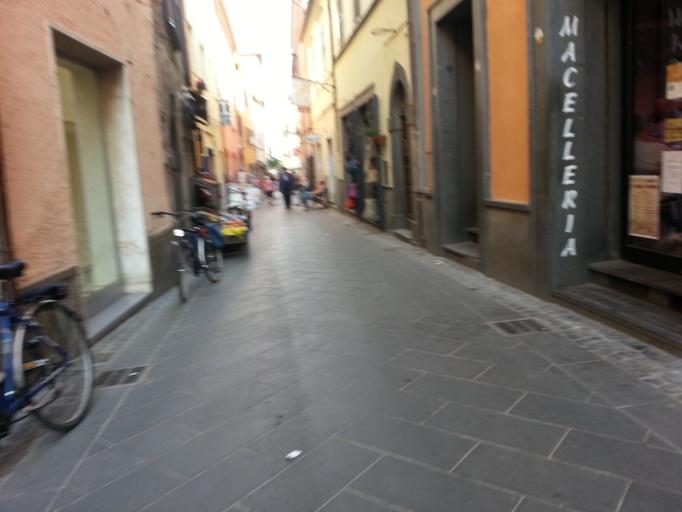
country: IT
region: Latium
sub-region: Provincia di Viterbo
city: Bolsena
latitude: 42.6443
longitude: 11.9876
